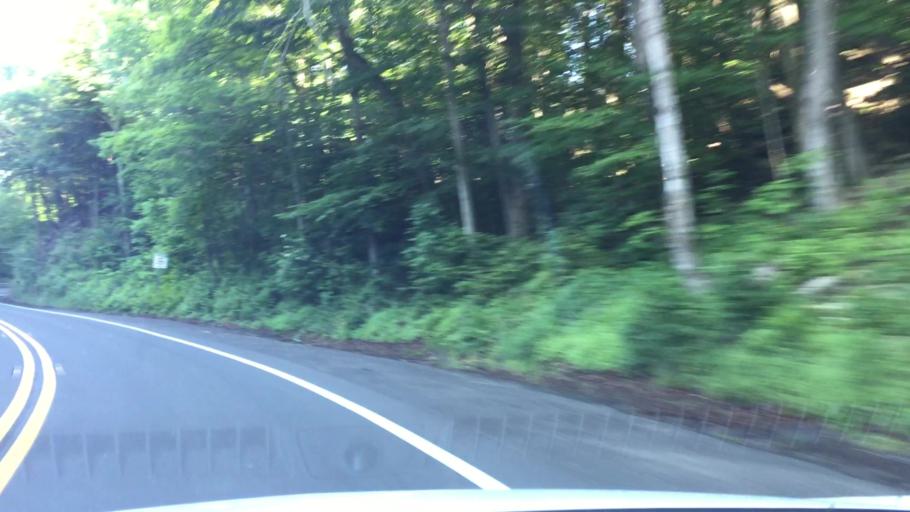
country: US
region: Massachusetts
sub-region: Berkshire County
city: Becket
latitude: 42.3172
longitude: -73.0933
